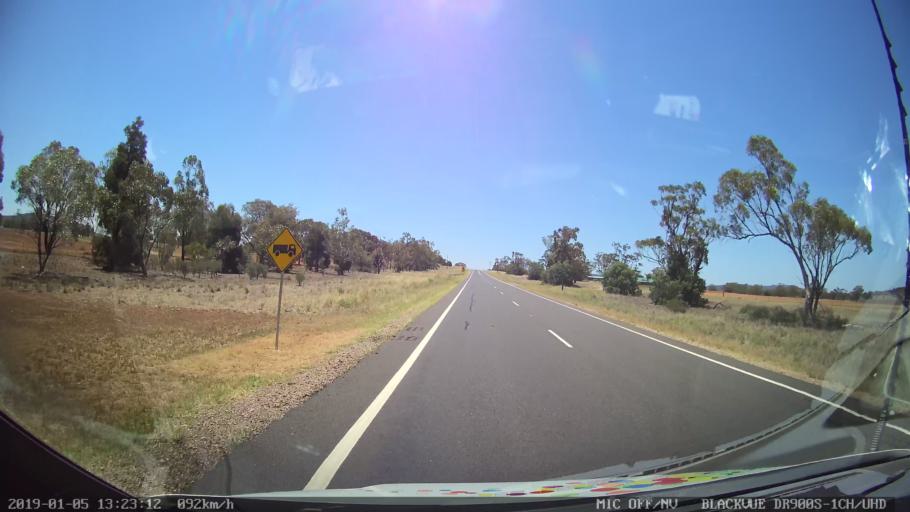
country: AU
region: New South Wales
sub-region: Gunnedah
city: Gunnedah
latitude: -31.0799
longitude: 149.9720
